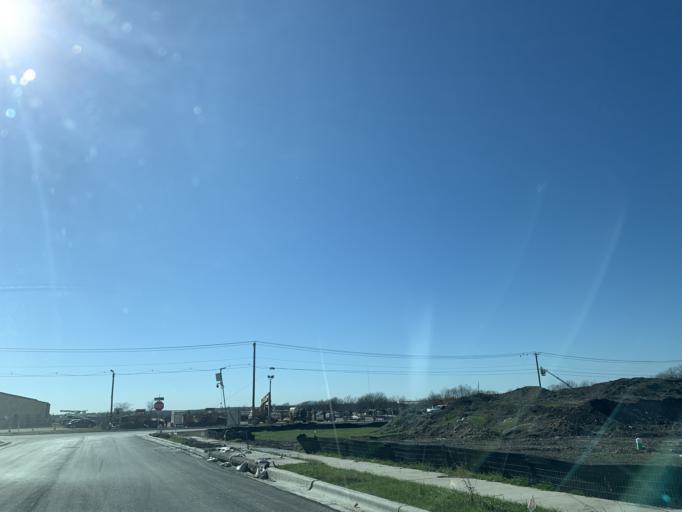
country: US
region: Texas
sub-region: Williamson County
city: Hutto
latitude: 30.5489
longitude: -97.5692
